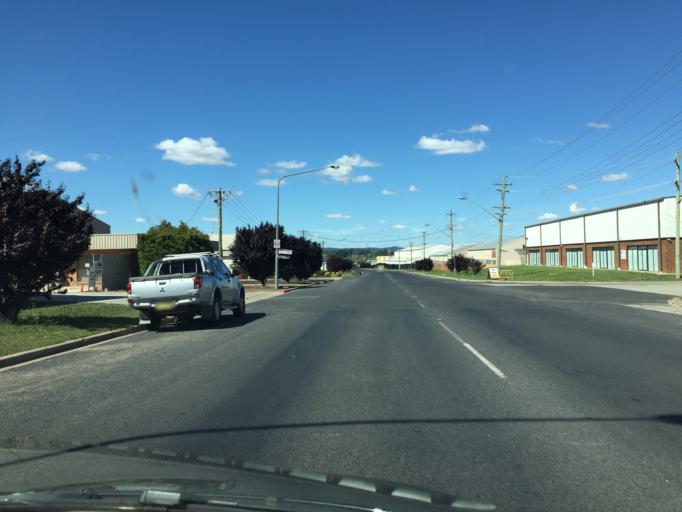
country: AU
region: Australian Capital Territory
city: Macarthur
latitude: -35.3898
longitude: 149.1688
